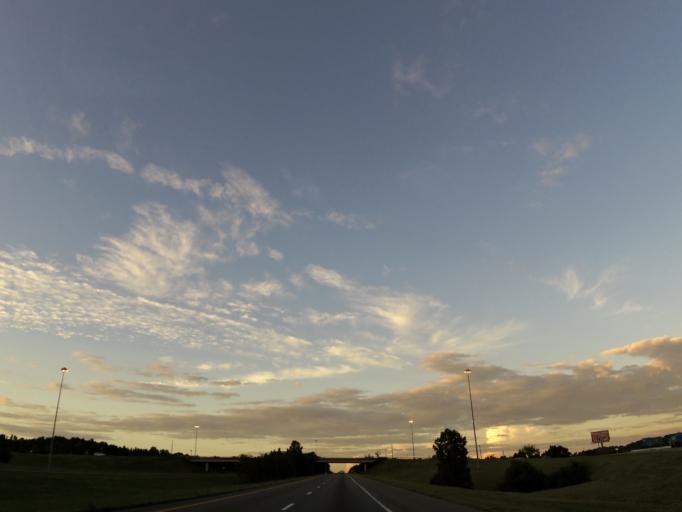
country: US
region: Tennessee
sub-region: McMinn County
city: Athens
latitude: 35.5017
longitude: -84.6124
